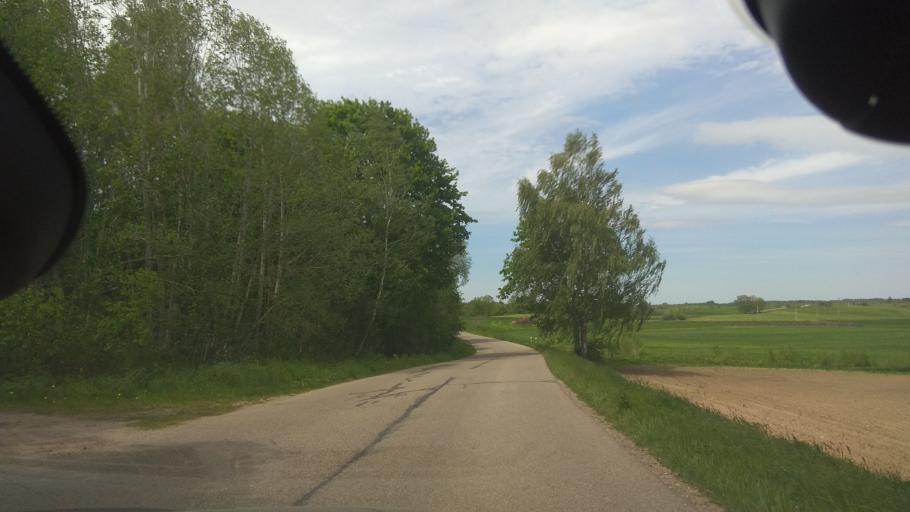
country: LT
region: Vilnius County
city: Ukmerge
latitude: 55.1511
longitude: 24.5501
